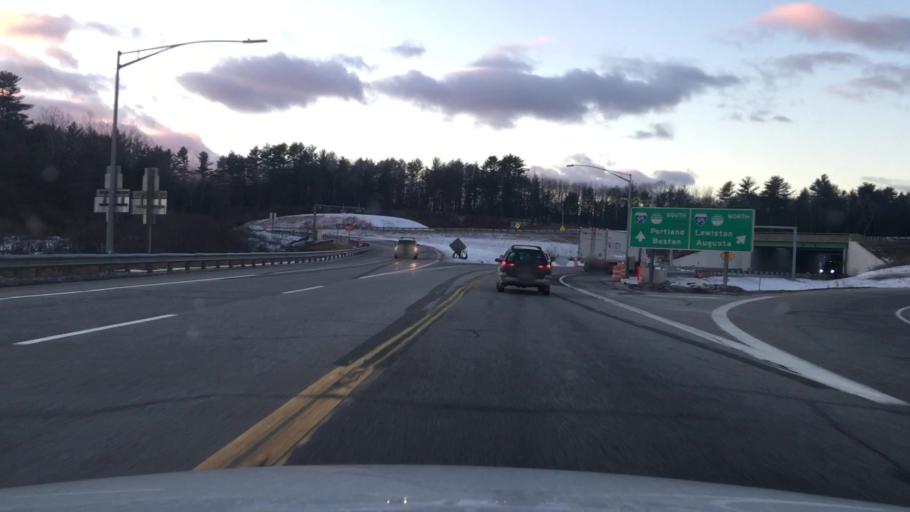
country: US
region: Maine
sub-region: Androscoggin County
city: Auburn
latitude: 44.0368
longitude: -70.2671
